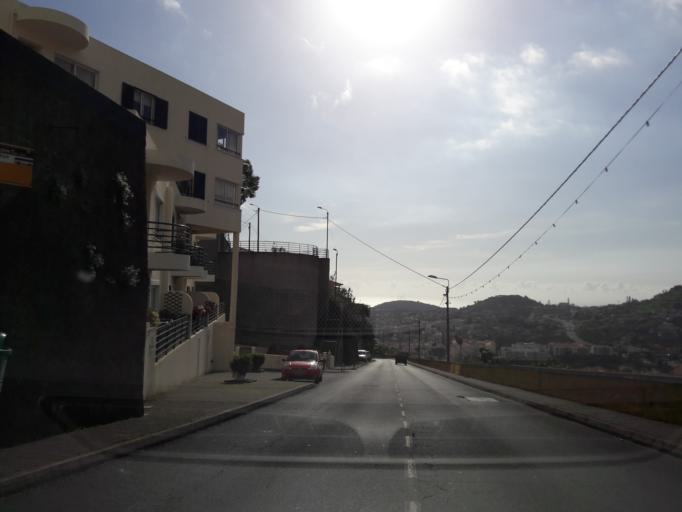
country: PT
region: Madeira
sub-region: Funchal
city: Nossa Senhora do Monte
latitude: 32.6681
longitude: -16.9247
